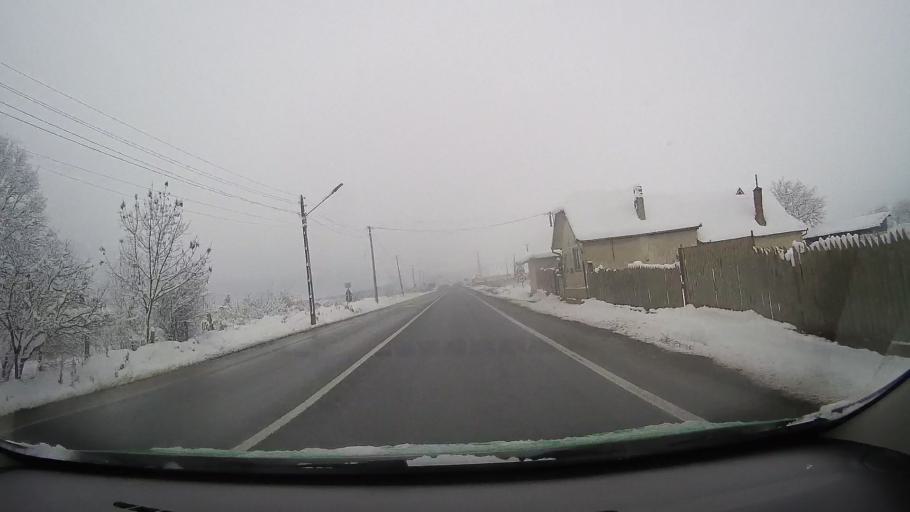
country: RO
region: Sibiu
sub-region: Comuna Orlat
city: Orlat
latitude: 45.7829
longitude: 23.9421
